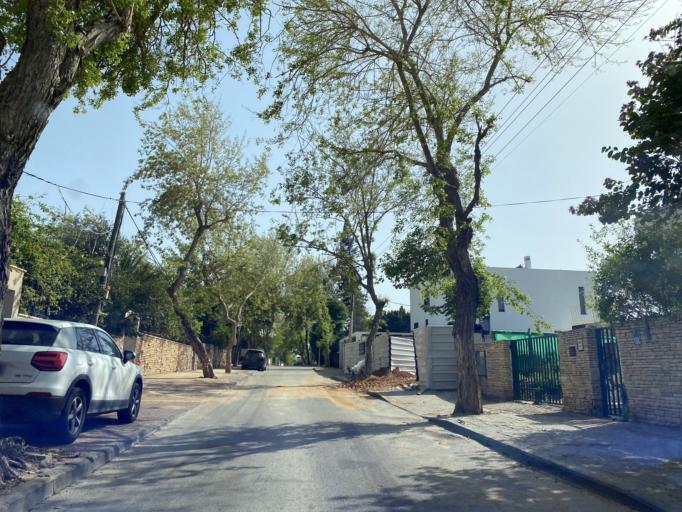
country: IL
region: Tel Aviv
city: Herzliya Pituah
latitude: 32.1765
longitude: 34.8071
